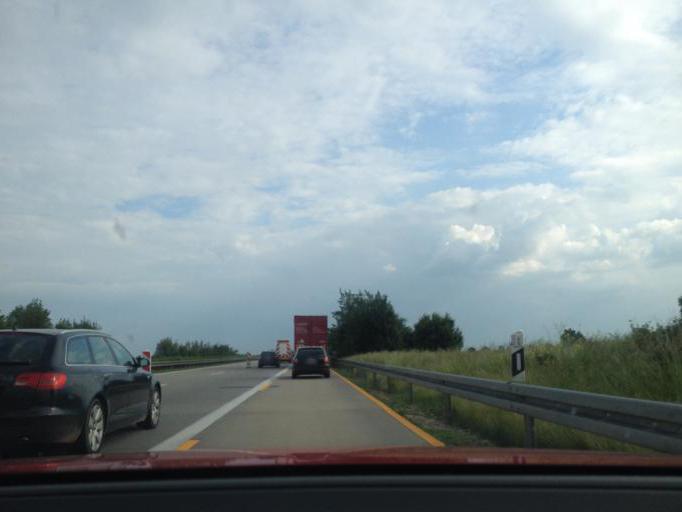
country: DE
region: Saxony-Anhalt
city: Nauendorf
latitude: 51.6072
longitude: 11.8702
